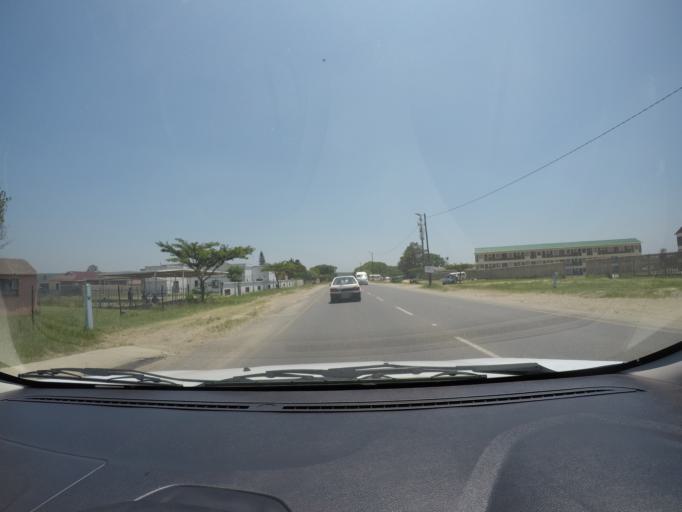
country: ZA
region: KwaZulu-Natal
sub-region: uThungulu District Municipality
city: eSikhawini
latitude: -28.8819
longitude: 31.9030
